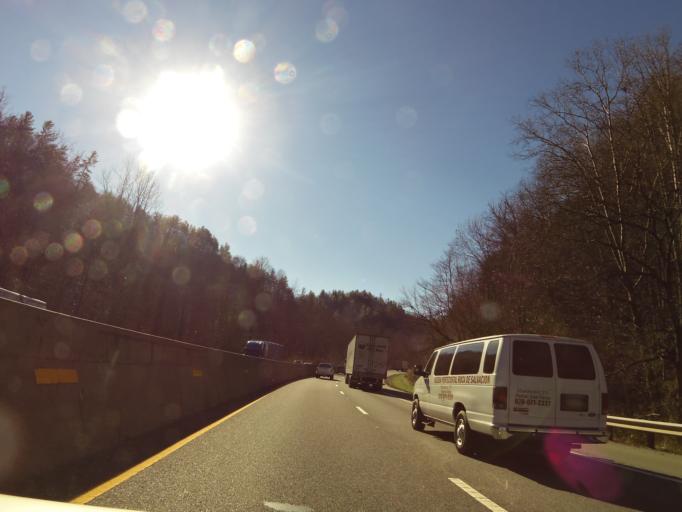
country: US
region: North Carolina
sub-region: Haywood County
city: Cove Creek
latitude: 35.6615
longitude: -82.9898
